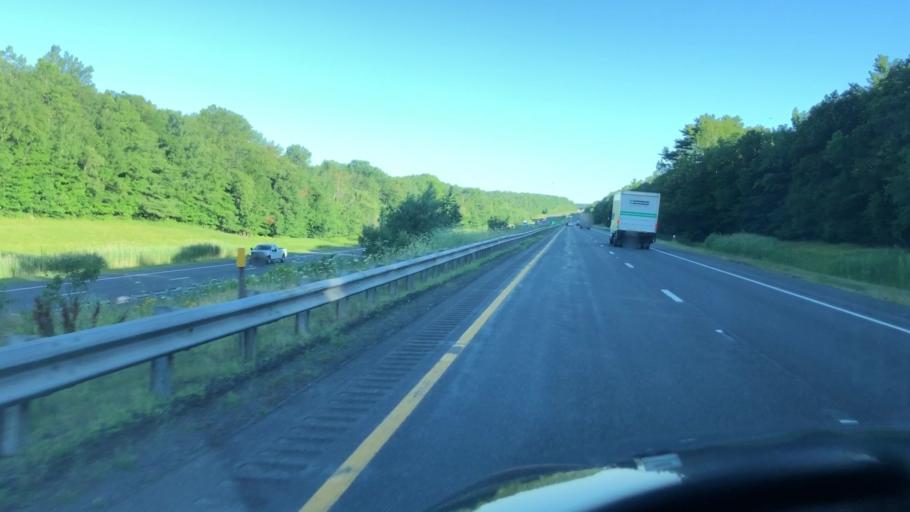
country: US
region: Massachusetts
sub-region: Berkshire County
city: Otis
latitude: 42.2073
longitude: -72.9486
